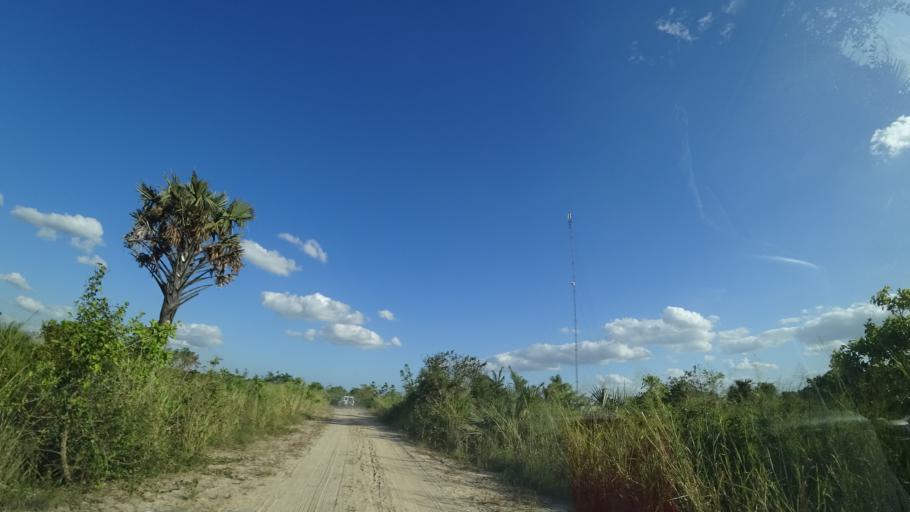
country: MZ
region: Sofala
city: Dondo
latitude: -19.3778
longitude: 34.5919
